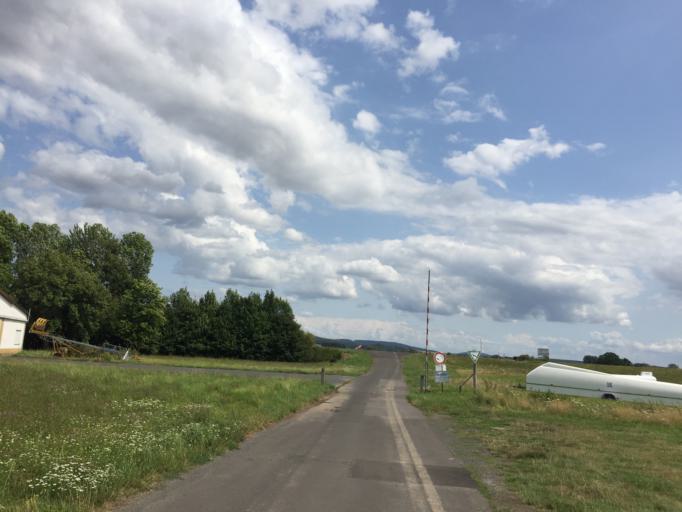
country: DE
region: Hesse
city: Schwalmstadt
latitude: 50.9056
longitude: 9.2364
